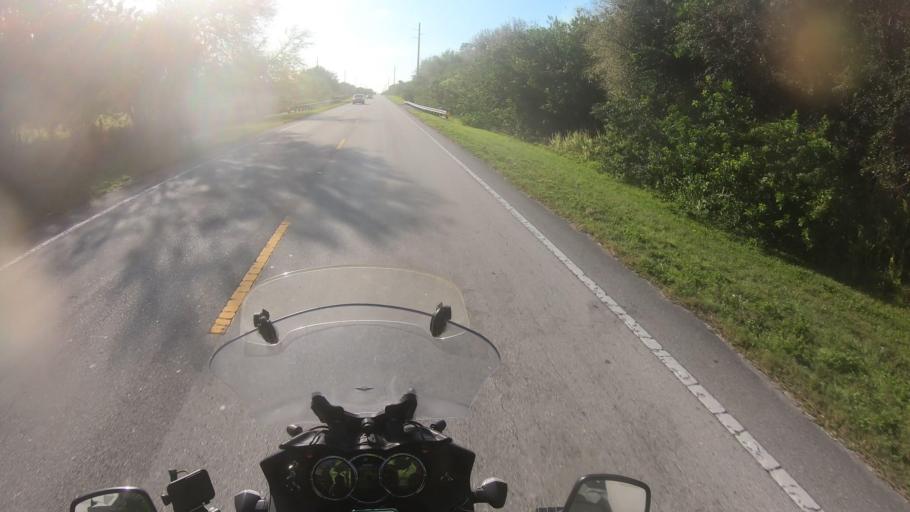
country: US
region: Florida
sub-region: Highlands County
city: Placid Lakes
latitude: 27.2090
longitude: -81.3825
